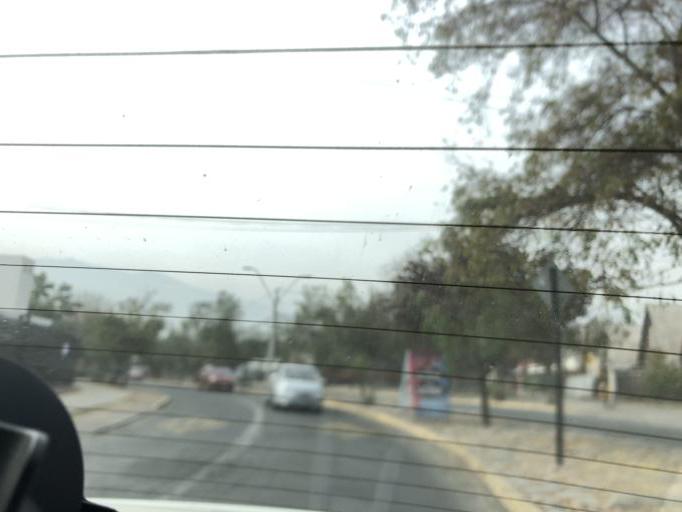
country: CL
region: Santiago Metropolitan
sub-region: Provincia de Cordillera
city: Puente Alto
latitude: -33.5933
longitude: -70.5685
